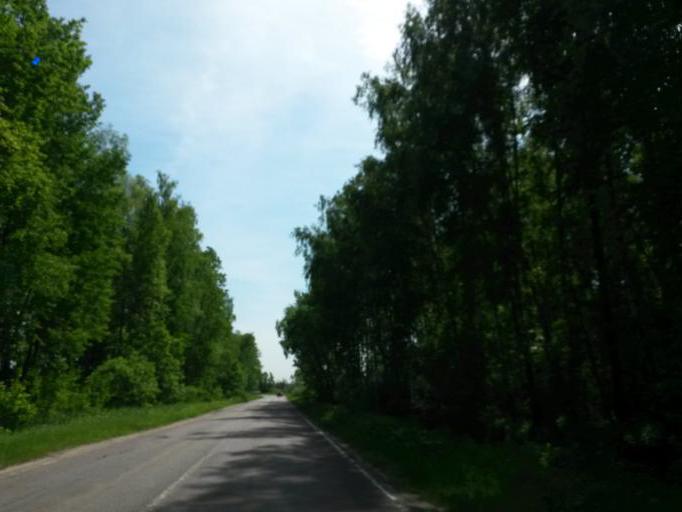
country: RU
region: Moskovskaya
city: Melikhovo
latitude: 55.1993
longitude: 37.6916
